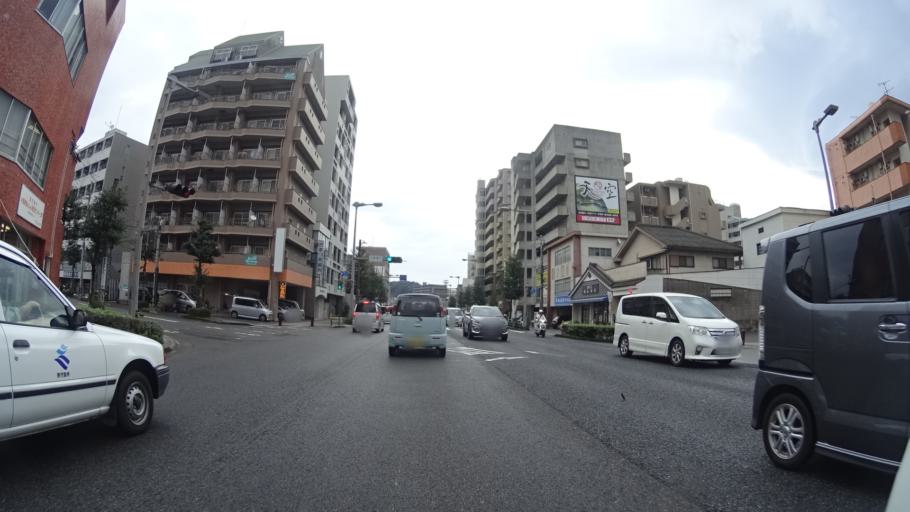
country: JP
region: Kagoshima
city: Kagoshima-shi
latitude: 31.6035
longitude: 130.5622
